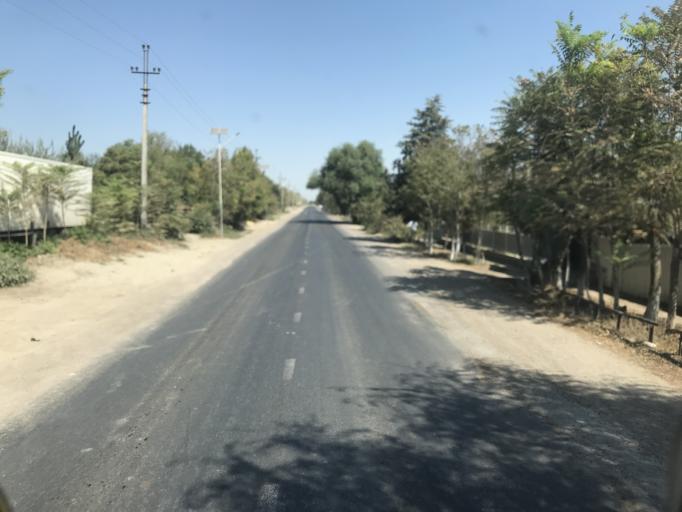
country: KZ
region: Ongtustik Qazaqstan
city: Ilyich
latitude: 40.9351
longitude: 68.4883
